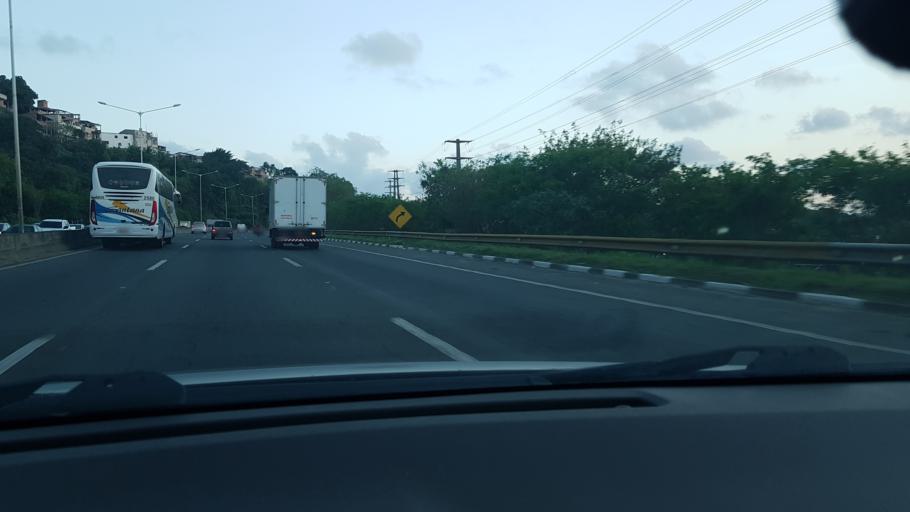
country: BR
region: Bahia
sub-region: Salvador
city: Salvador
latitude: -12.9456
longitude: -38.4701
